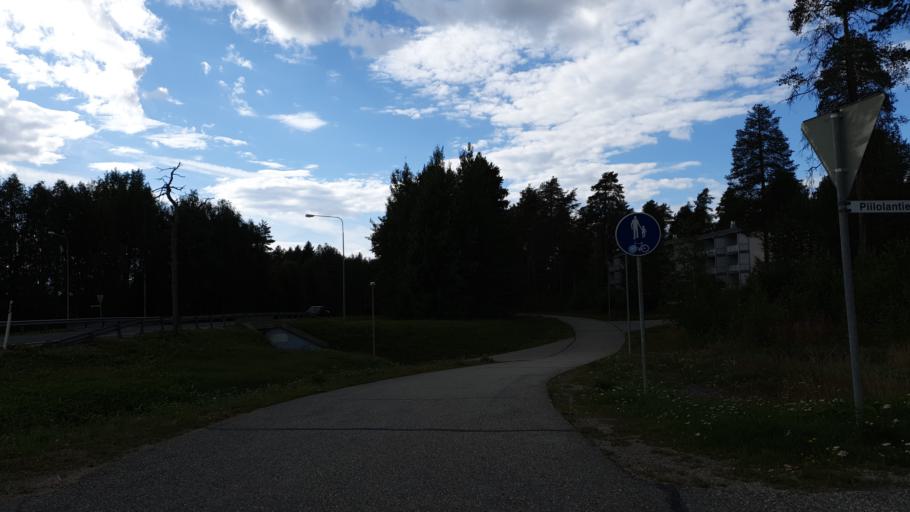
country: FI
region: Kainuu
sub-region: Kehys-Kainuu
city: Kuhmo
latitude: 64.1205
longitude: 29.5174
